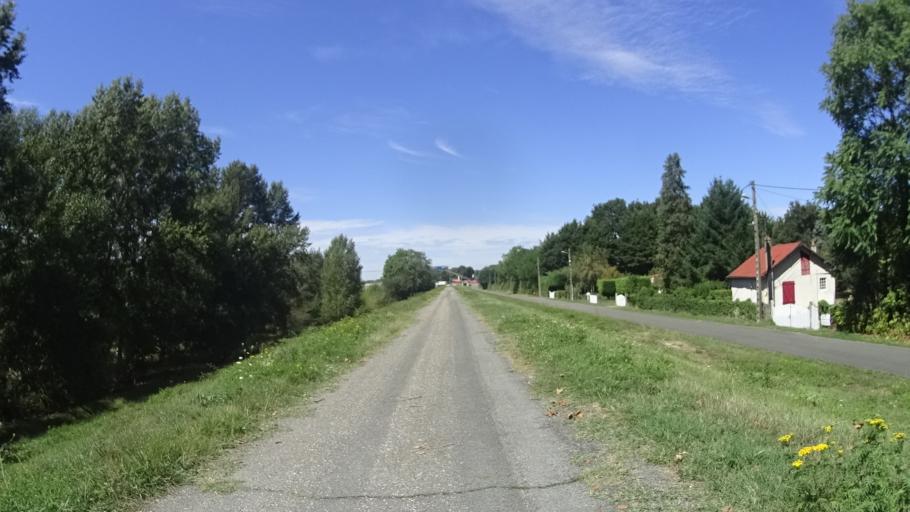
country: FR
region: Centre
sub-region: Departement du Loiret
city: Briare
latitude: 47.5969
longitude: 2.7664
